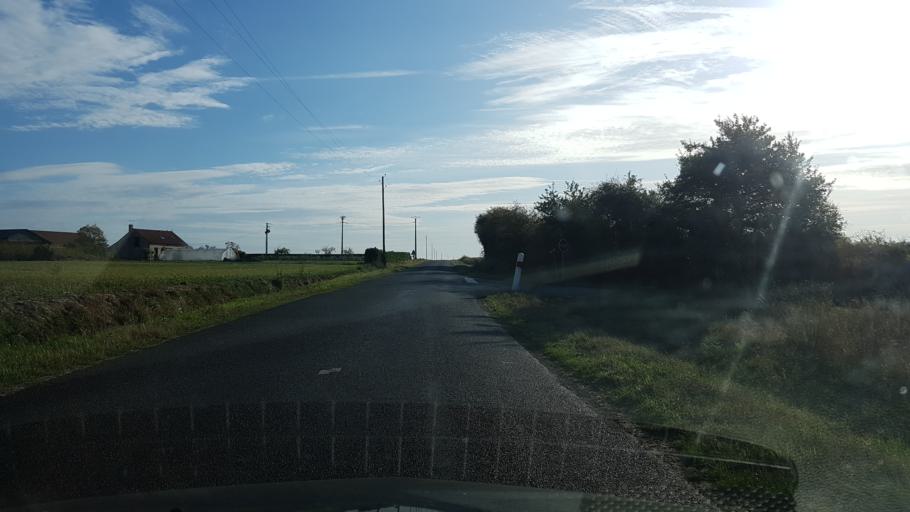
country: FR
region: Centre
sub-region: Departement du Loiret
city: Dampierre-en-Burly
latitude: 47.6964
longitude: 2.5050
